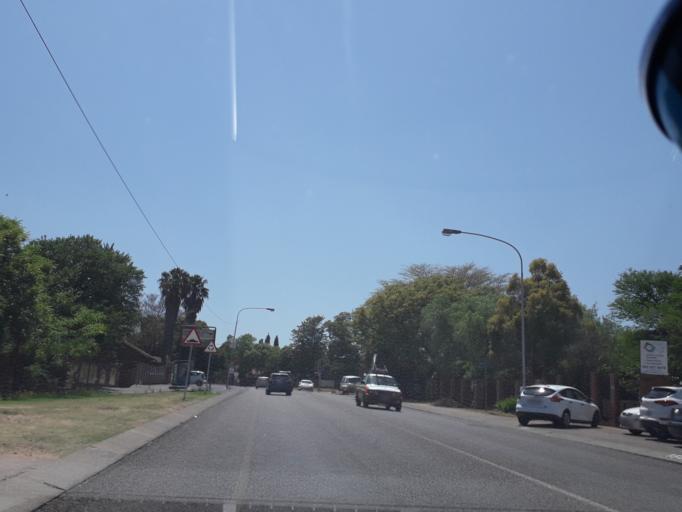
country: ZA
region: Gauteng
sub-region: City of Tshwane Metropolitan Municipality
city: Centurion
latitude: -25.8936
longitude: 28.1451
